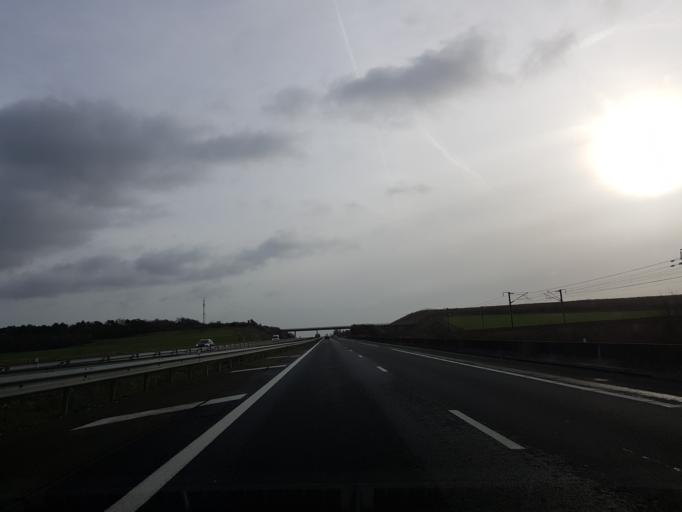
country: FR
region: Bourgogne
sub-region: Departement de l'Yonne
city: Courlon-sur-Yonne
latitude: 48.3453
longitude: 3.1882
